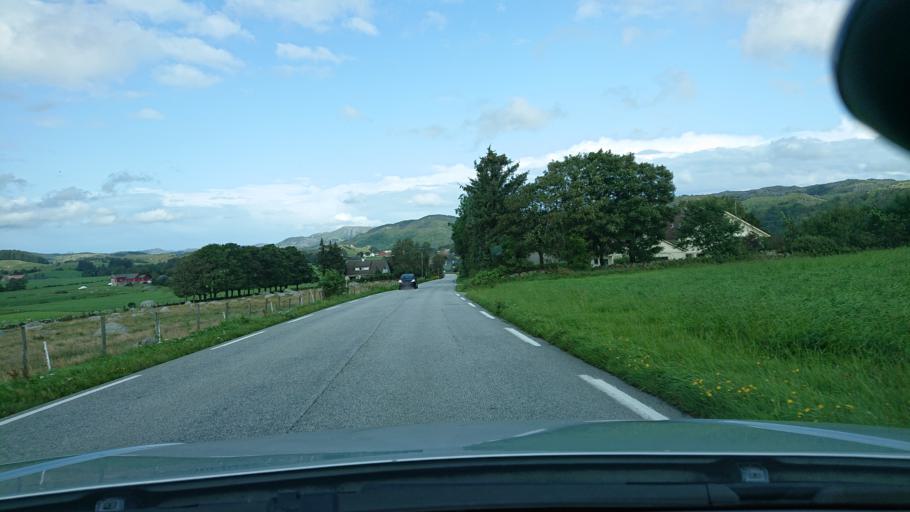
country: NO
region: Rogaland
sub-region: Gjesdal
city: Algard
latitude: 58.6942
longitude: 5.7761
